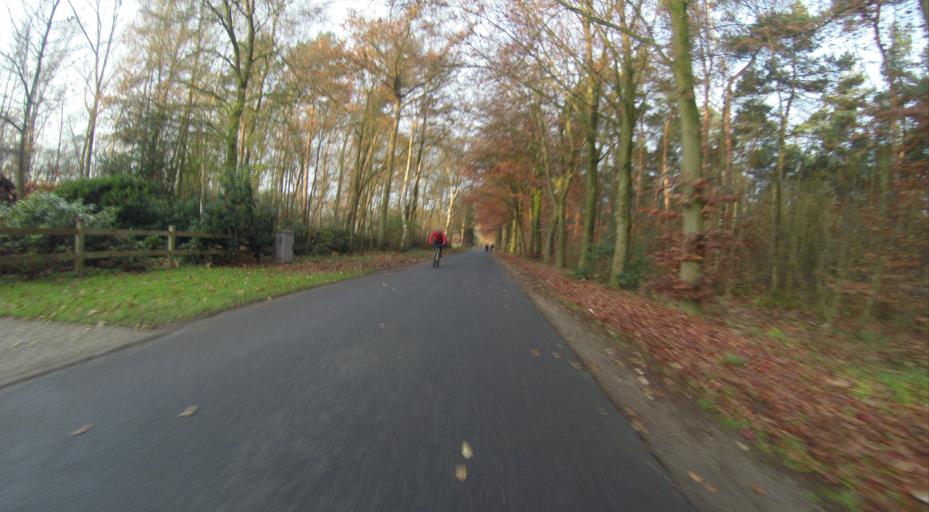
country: NL
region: Gelderland
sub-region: Gemeente Lochem
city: Almen
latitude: 52.1094
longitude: 6.3347
